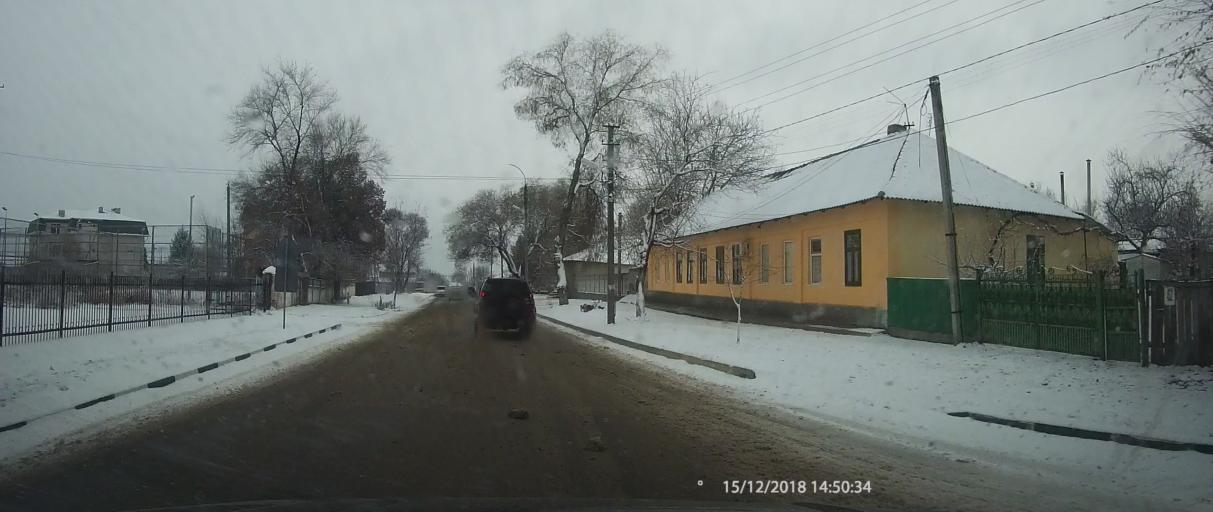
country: MD
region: Cahul
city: Cahul
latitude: 45.9009
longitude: 28.1873
